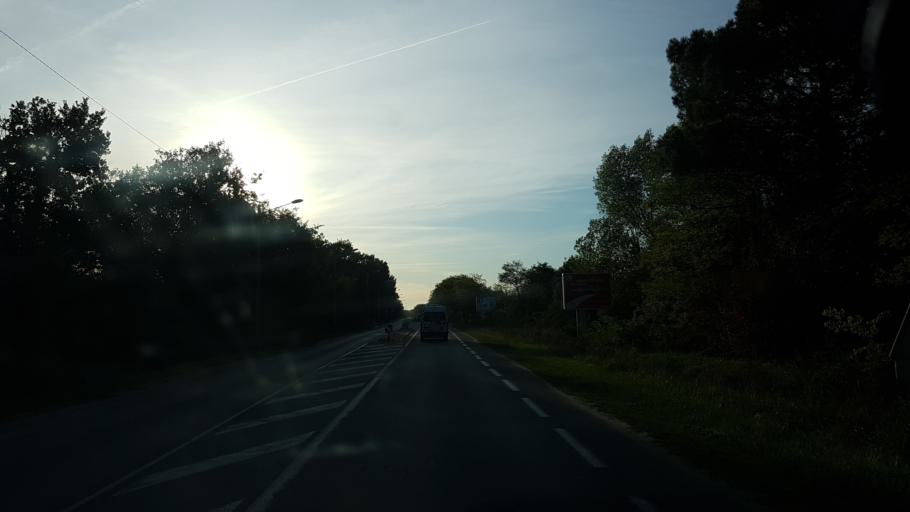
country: FR
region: Aquitaine
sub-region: Departement de la Gironde
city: Saint-Medard-en-Jalles
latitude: 44.8461
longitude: -0.7236
